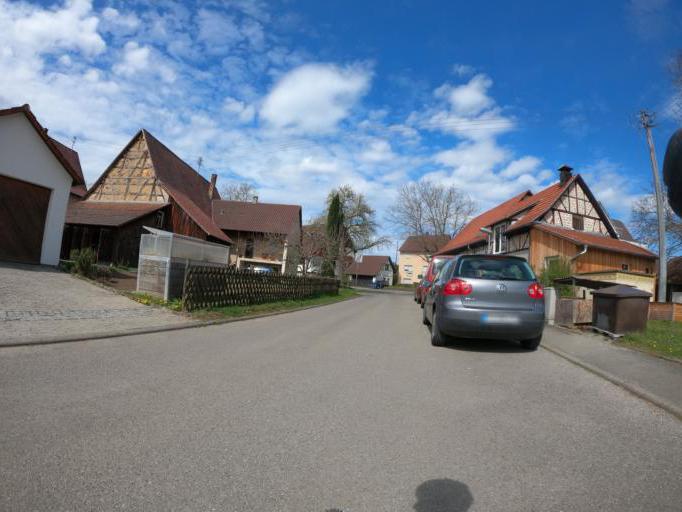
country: DE
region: Baden-Wuerttemberg
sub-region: Tuebingen Region
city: Gomaringen
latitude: 48.4823
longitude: 9.1033
